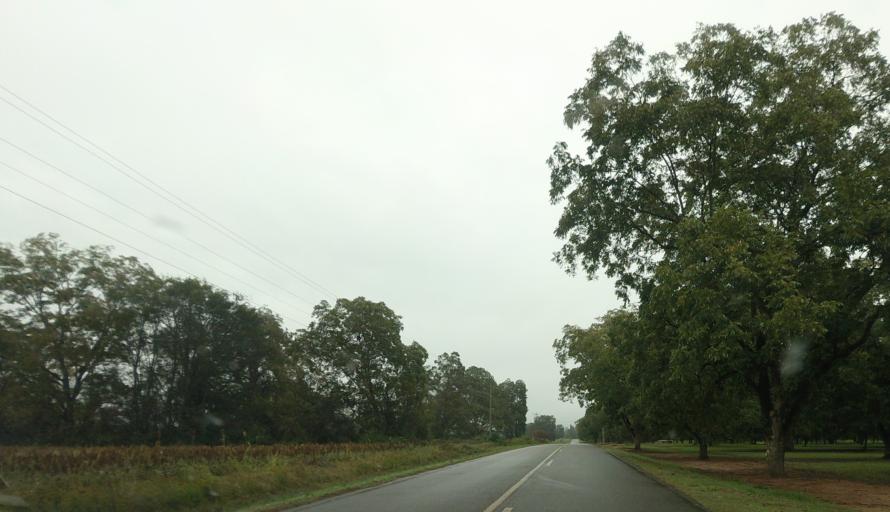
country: US
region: Georgia
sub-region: Peach County
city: Fort Valley
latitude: 32.5303
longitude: -83.9595
